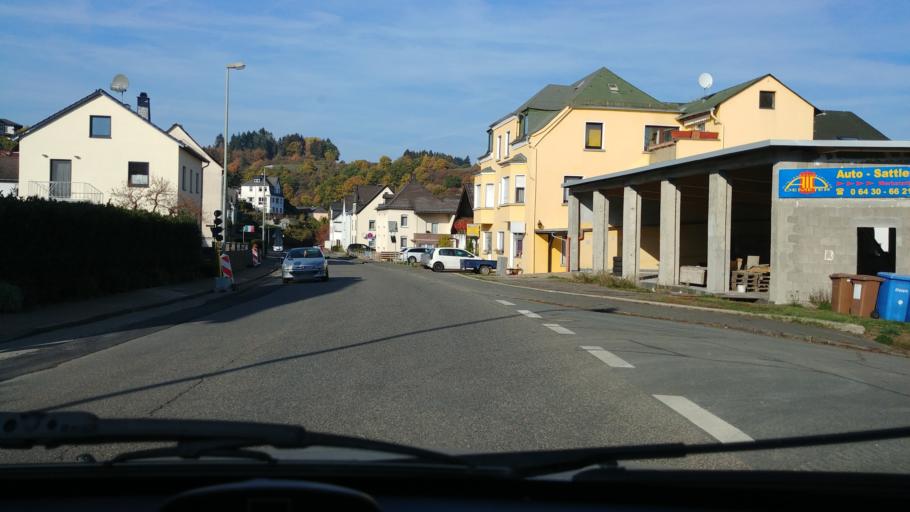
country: DE
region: Rheinland-Pfalz
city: Schiesheim
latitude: 50.2623
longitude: 8.0533
